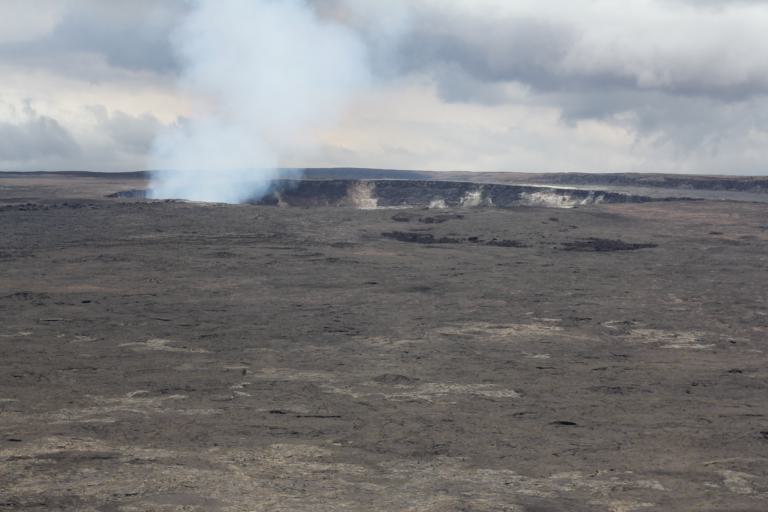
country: US
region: Hawaii
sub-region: Hawaii County
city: Volcano
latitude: 19.4299
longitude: -155.2671
